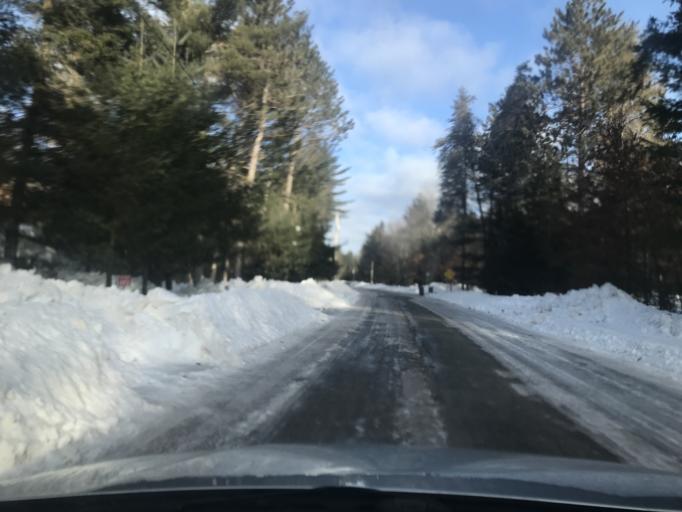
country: US
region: Wisconsin
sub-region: Marinette County
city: Niagara
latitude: 45.6346
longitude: -87.9687
